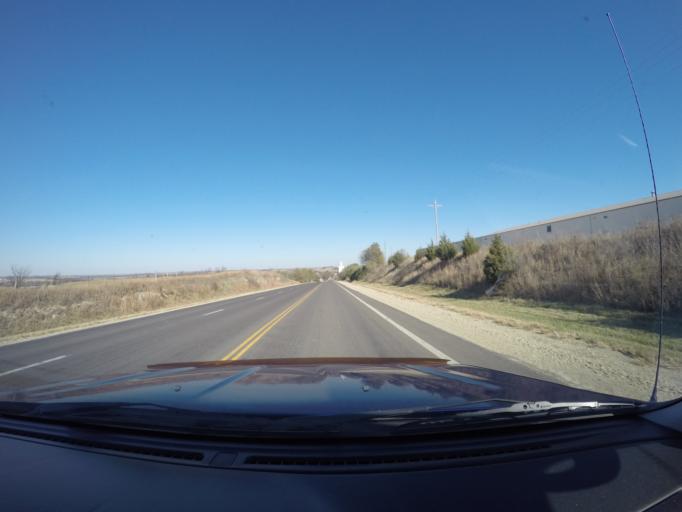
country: US
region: Kansas
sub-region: Marshall County
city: Blue Rapids
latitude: 39.6821
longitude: -96.7509
